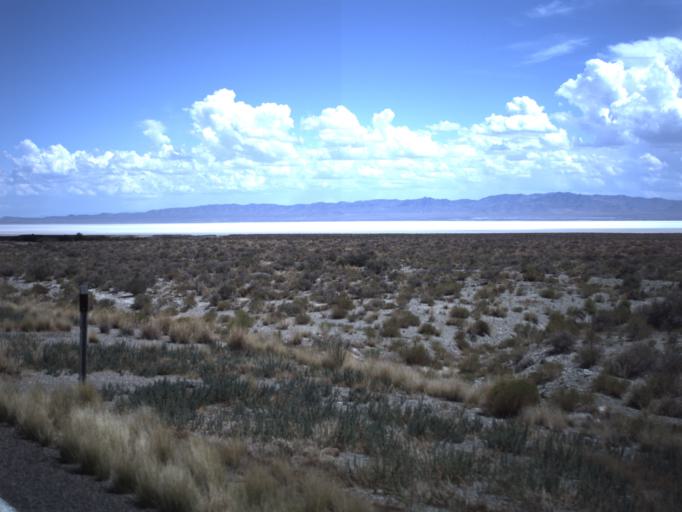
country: US
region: Utah
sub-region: Beaver County
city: Milford
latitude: 39.0609
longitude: -113.2450
